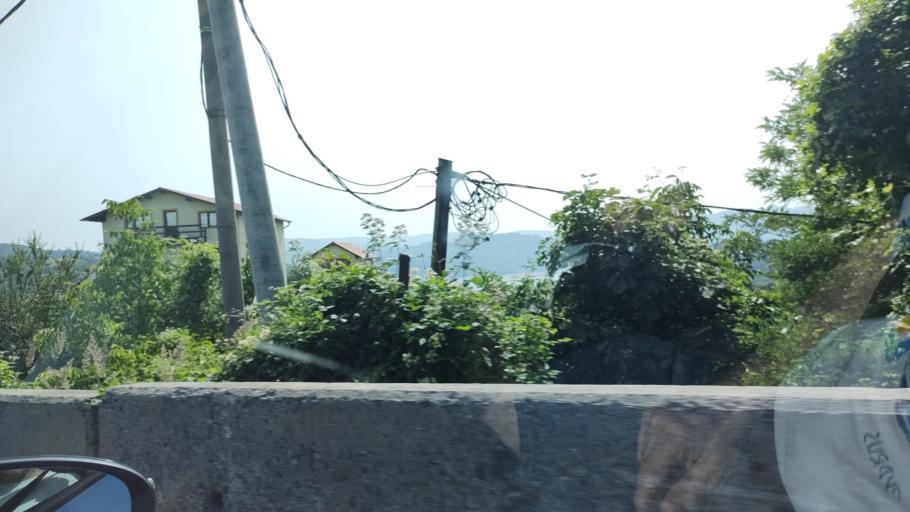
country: RO
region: Mehedinti
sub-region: Municipiul Orsova
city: Orsova
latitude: 44.7273
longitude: 22.3720
